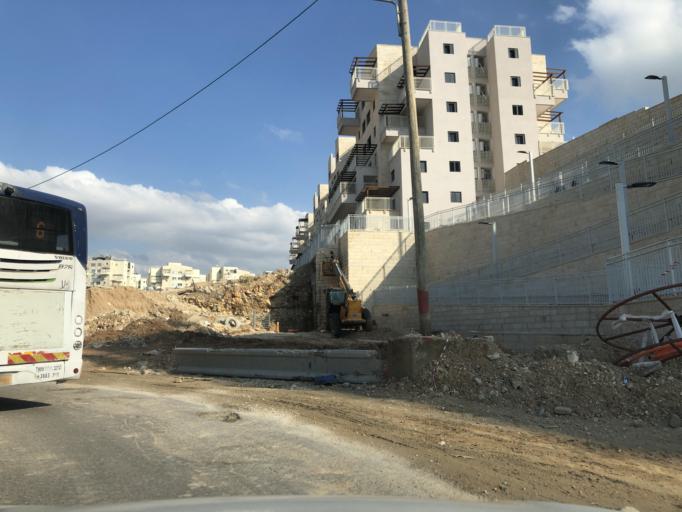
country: IL
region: Jerusalem
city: Modiin Ilit
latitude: 31.9338
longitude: 35.0497
